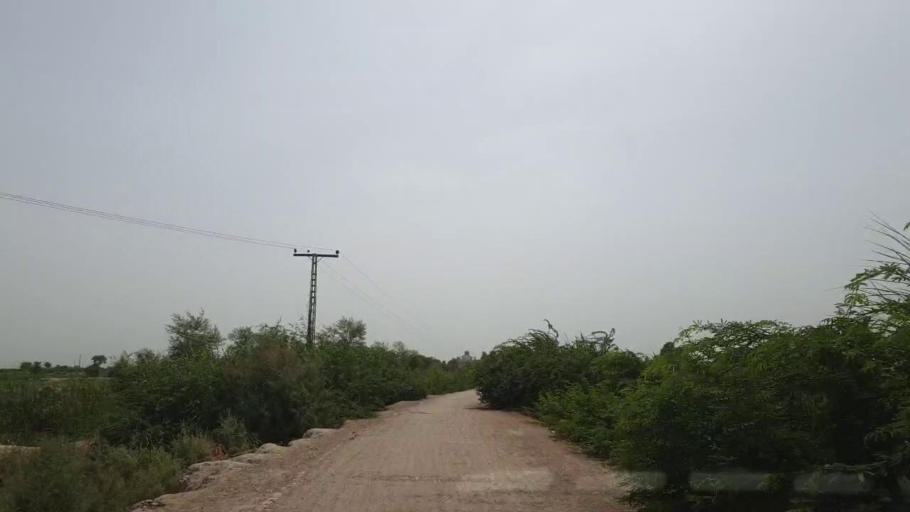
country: PK
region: Sindh
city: Sakrand
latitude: 26.1151
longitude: 68.2938
